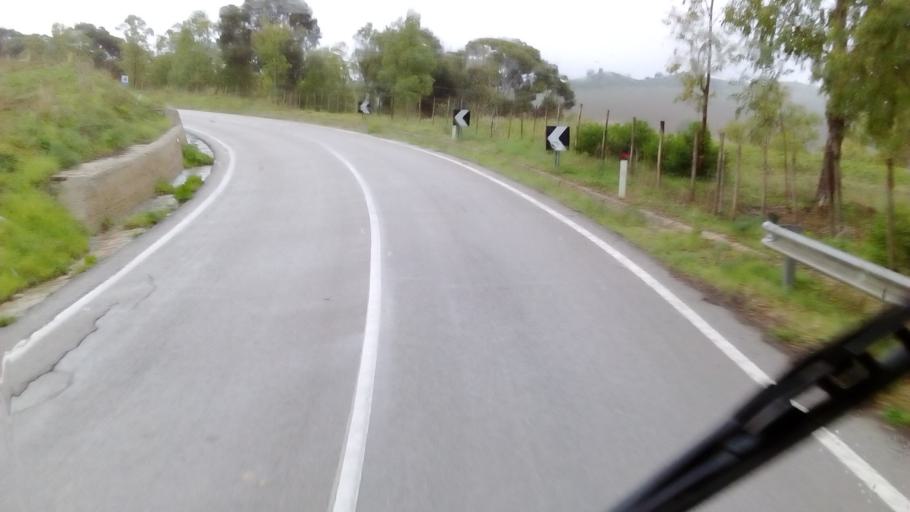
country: IT
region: Sicily
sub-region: Enna
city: Pietraperzia
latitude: 37.4656
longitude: 14.1730
